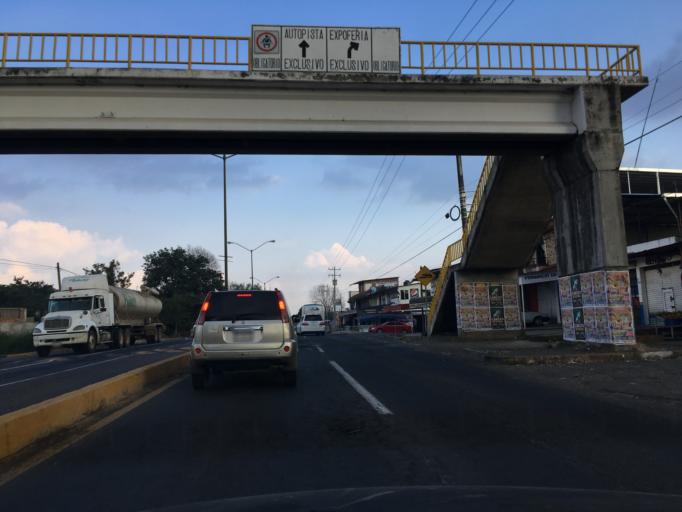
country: MX
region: Michoacan
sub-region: Uruapan
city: Toreo Bajo (El Toreo Bajo)
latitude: 19.4234
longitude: -102.0093
